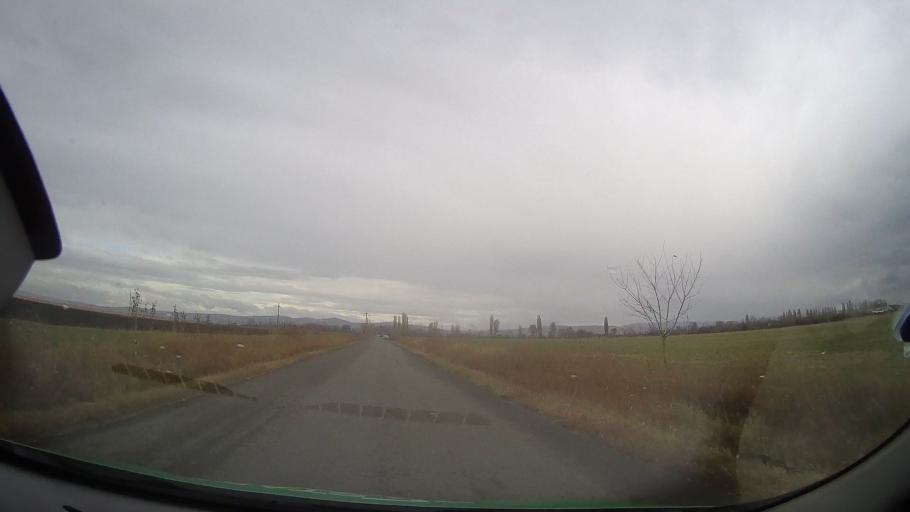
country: RO
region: Prahova
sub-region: Comuna Colceag
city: Inotesti
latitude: 44.9653
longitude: 26.3470
